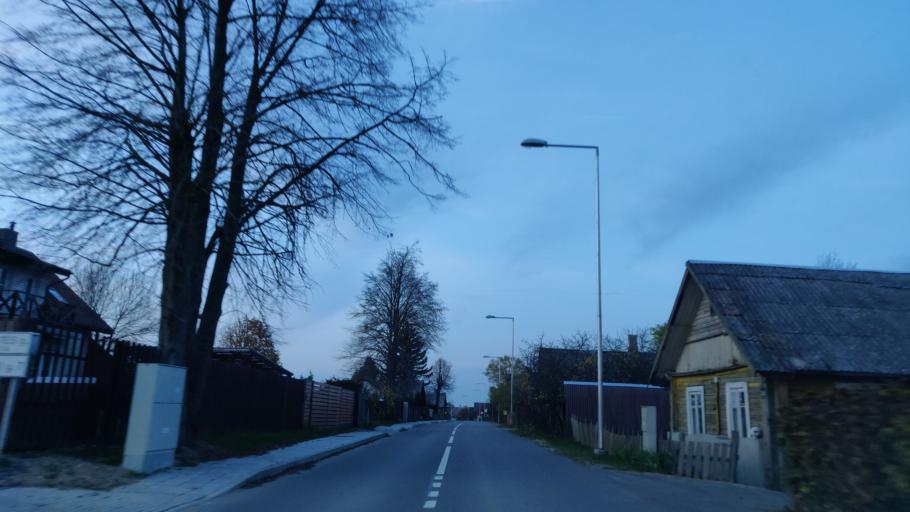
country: LT
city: Lentvaris
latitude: 54.5846
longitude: 25.0513
